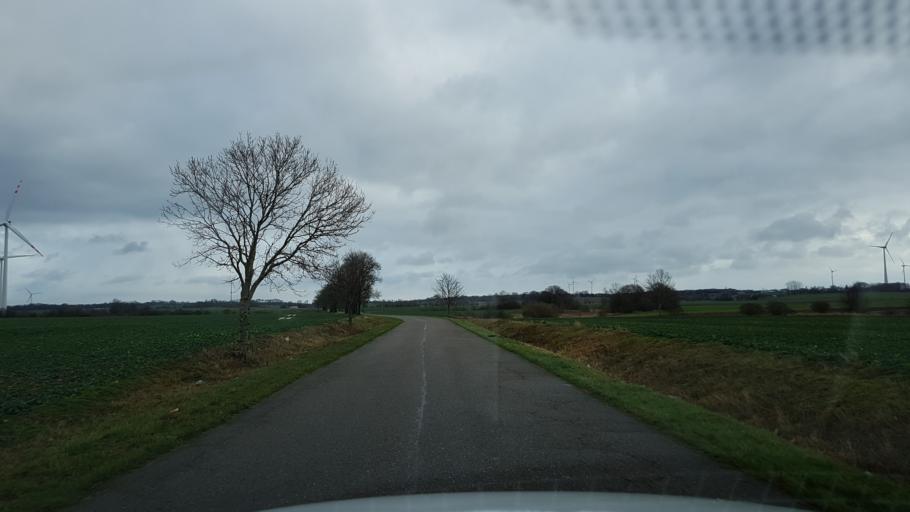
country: PL
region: West Pomeranian Voivodeship
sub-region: Powiat slawienski
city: Slawno
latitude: 54.5181
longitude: 16.6655
